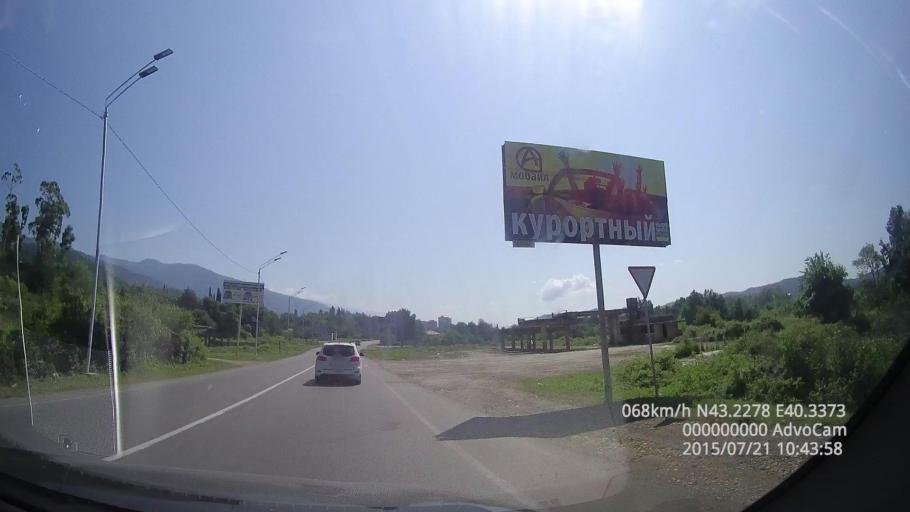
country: GE
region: Abkhazia
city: Bich'vinta
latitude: 43.2279
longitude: 40.3374
